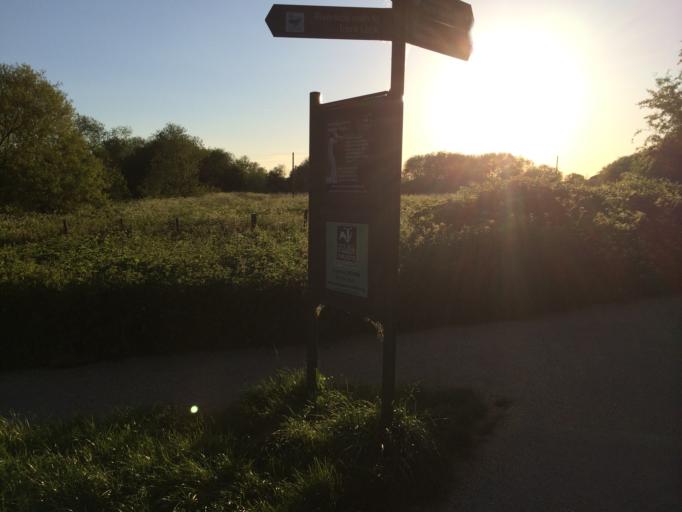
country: GB
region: England
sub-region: Nottinghamshire
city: Gotham
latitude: 52.8966
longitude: -1.2290
